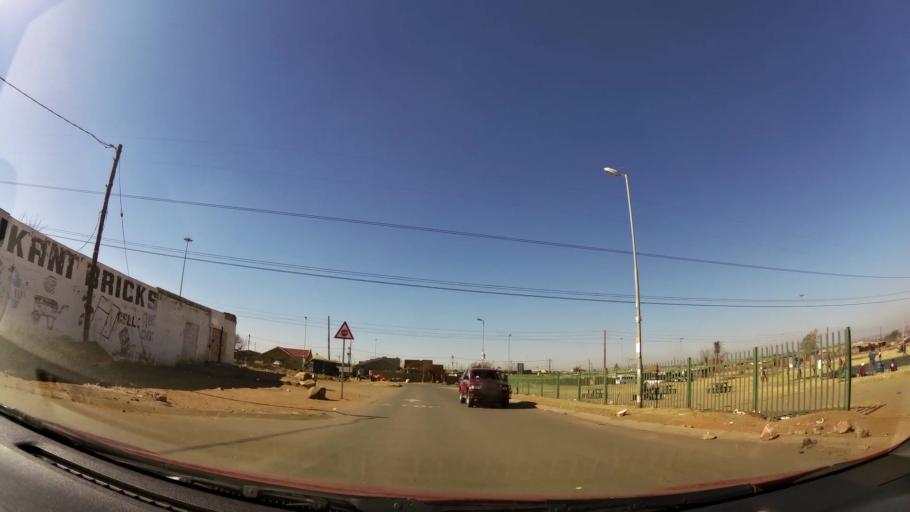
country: ZA
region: Gauteng
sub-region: City of Johannesburg Metropolitan Municipality
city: Soweto
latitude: -26.2207
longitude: 27.8198
